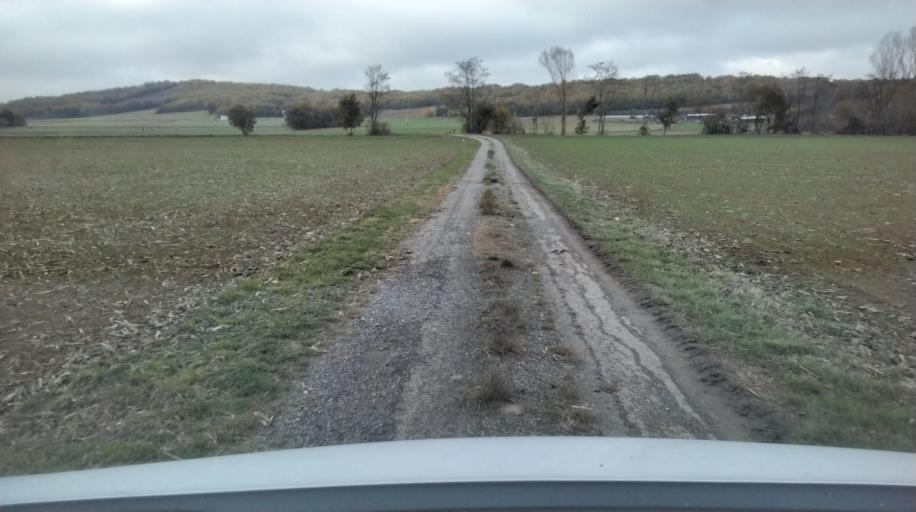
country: FR
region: Midi-Pyrenees
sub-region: Departement de la Haute-Garonne
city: Le Fousseret
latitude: 43.2694
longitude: 1.0438
